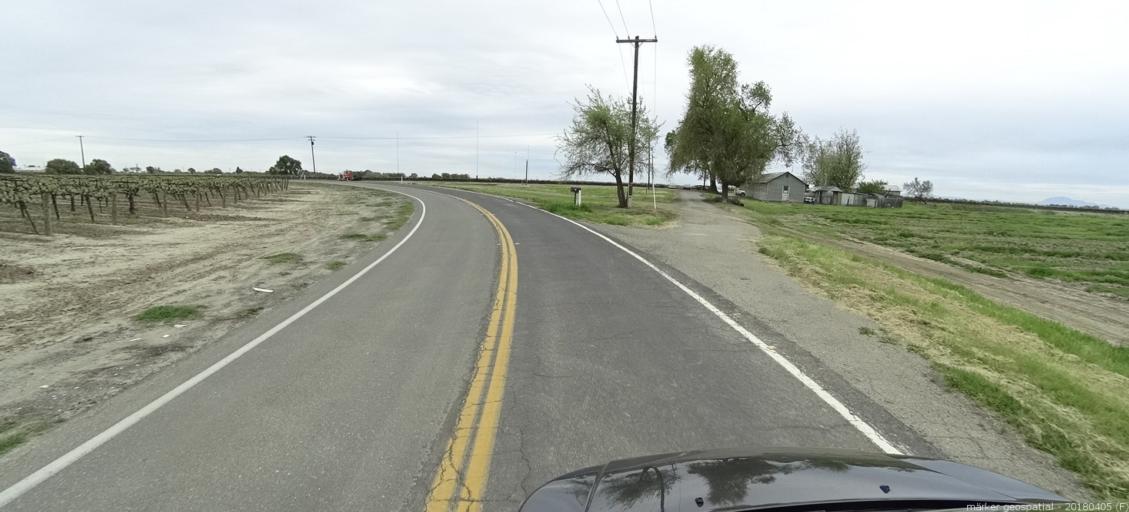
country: US
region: California
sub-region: Sacramento County
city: Walnut Grove
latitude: 38.3218
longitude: -121.5280
